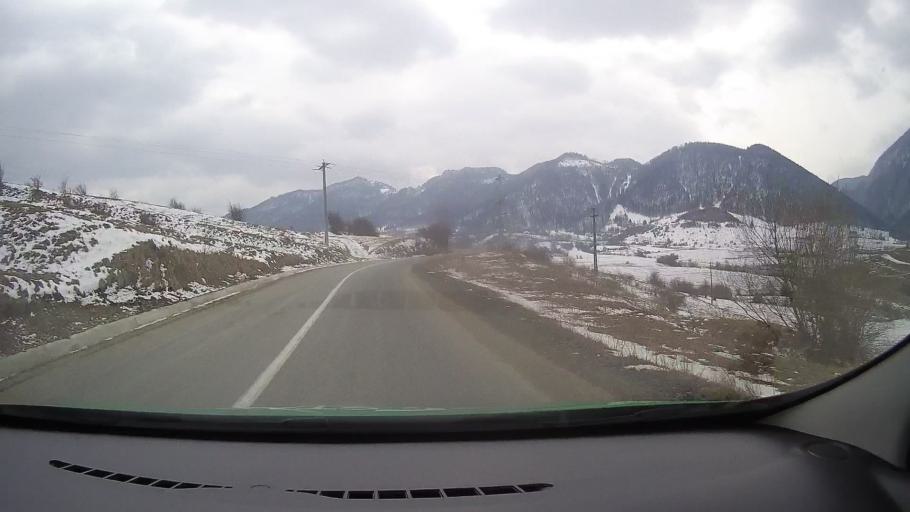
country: RO
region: Brasov
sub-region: Comuna Zarnesti
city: Zarnesti
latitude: 45.5531
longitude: 25.3197
